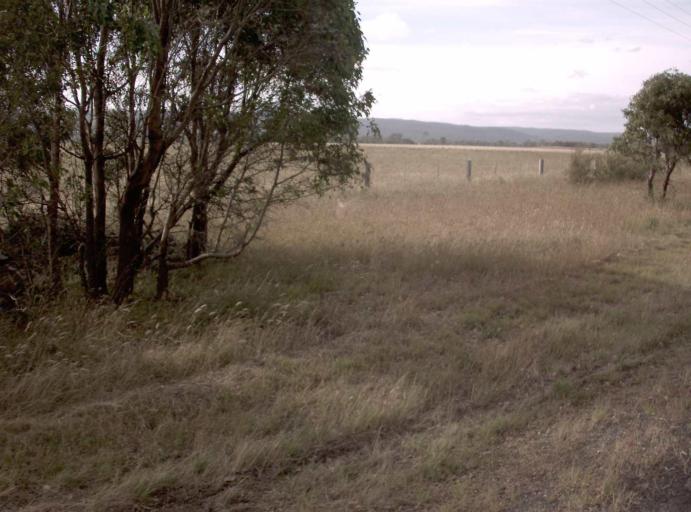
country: AU
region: Victoria
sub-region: Wellington
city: Heyfield
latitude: -38.0567
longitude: 146.6625
